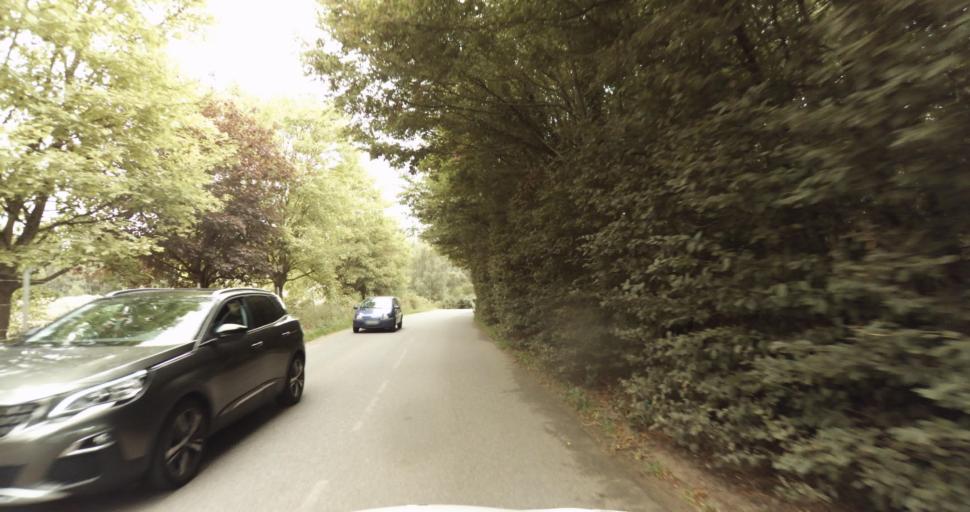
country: FR
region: Haute-Normandie
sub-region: Departement de l'Eure
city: Gravigny
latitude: 49.0383
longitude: 1.1738
